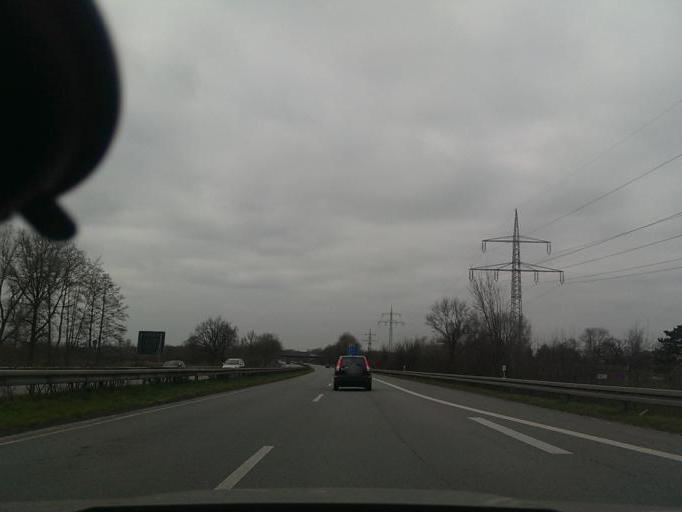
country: DE
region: North Rhine-Westphalia
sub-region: Regierungsbezirk Detmold
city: Rheda-Wiedenbruck
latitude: 51.8381
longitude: 8.3368
